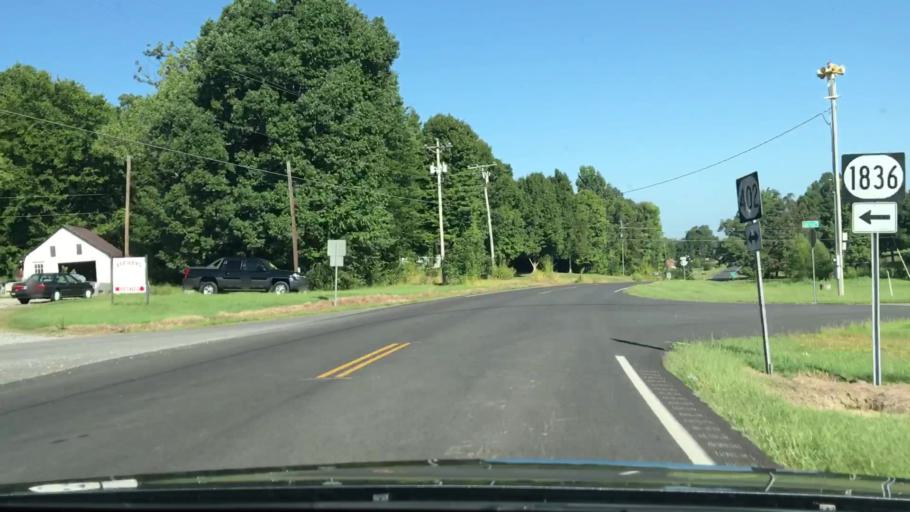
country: US
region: Kentucky
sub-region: Marshall County
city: Benton
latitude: 36.7695
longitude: -88.4389
